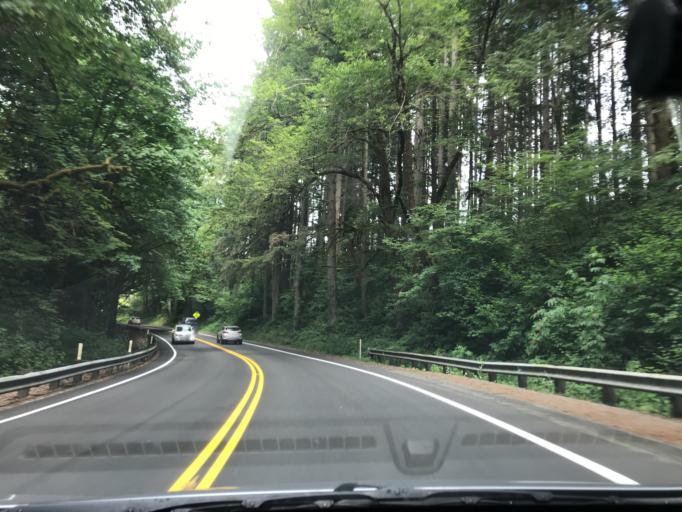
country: US
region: Washington
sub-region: King County
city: Lake Morton-Berrydale
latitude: 47.3173
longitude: -122.1317
